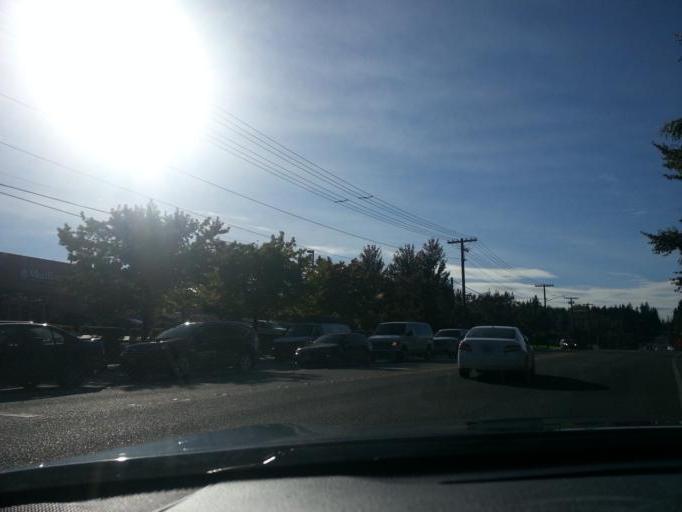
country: US
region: Washington
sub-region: King County
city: Bothell
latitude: 47.7915
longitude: -122.2133
